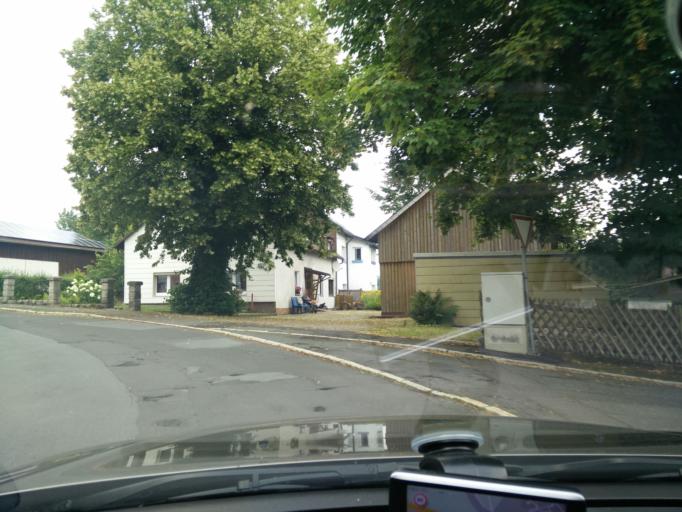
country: DE
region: Bavaria
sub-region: Upper Franconia
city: Mehlmeisel
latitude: 49.9769
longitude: 11.8557
